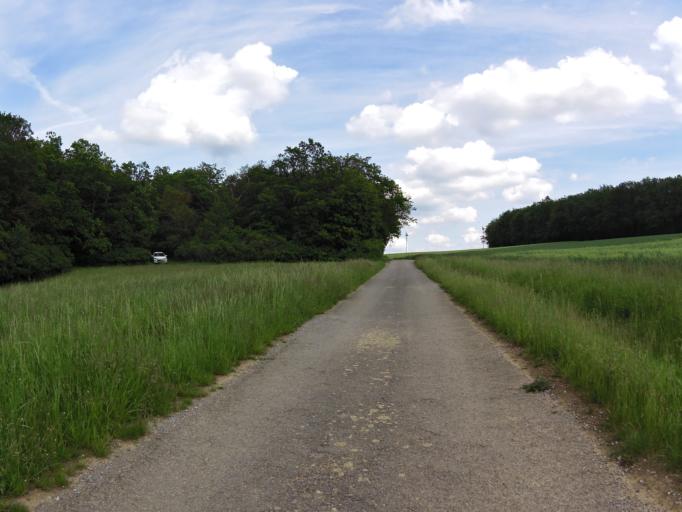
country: DE
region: Bavaria
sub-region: Regierungsbezirk Unterfranken
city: Sommerhausen
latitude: 49.7183
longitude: 10.0273
